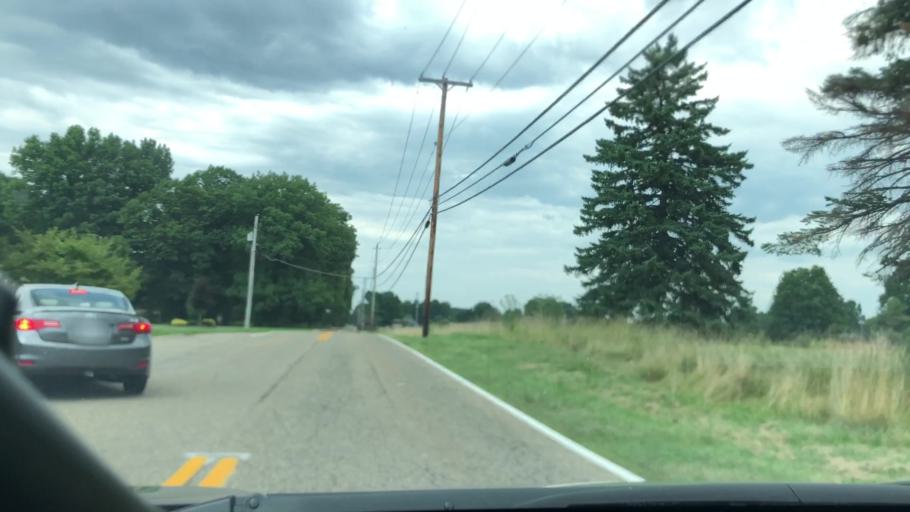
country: US
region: Ohio
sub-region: Summit County
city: New Franklin
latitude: 40.8897
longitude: -81.5182
